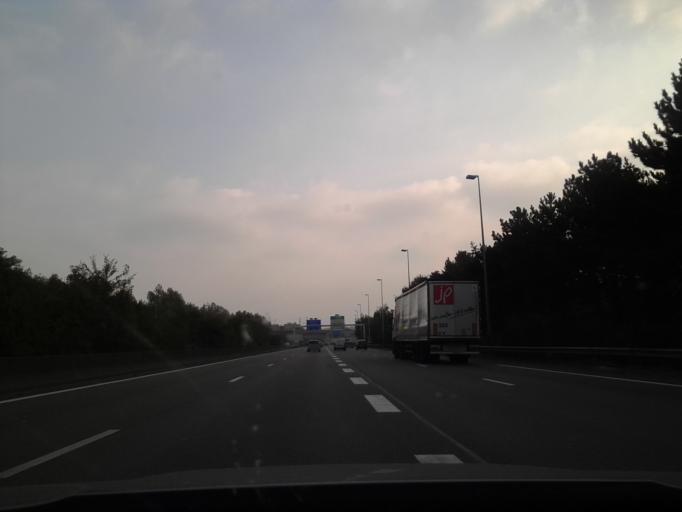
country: FR
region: Nord-Pas-de-Calais
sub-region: Departement du Nord
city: Lezennes
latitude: 50.6000
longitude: 3.1135
